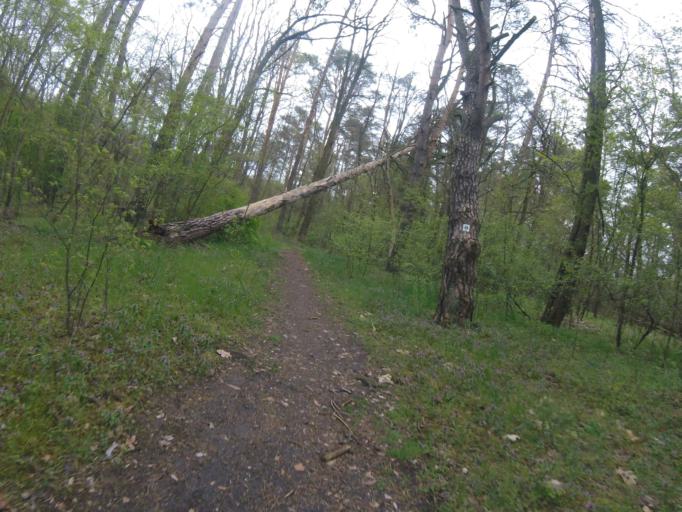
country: DE
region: Brandenburg
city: Bestensee
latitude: 52.2420
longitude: 13.6745
